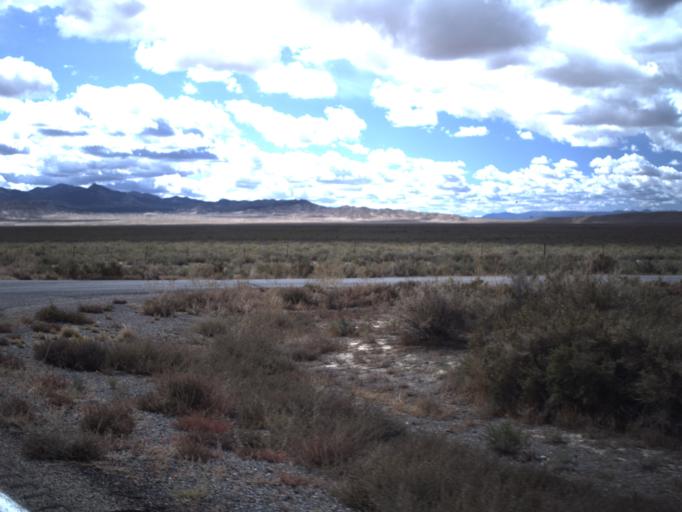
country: US
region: Nevada
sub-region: White Pine County
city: McGill
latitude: 38.8091
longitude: -113.9805
